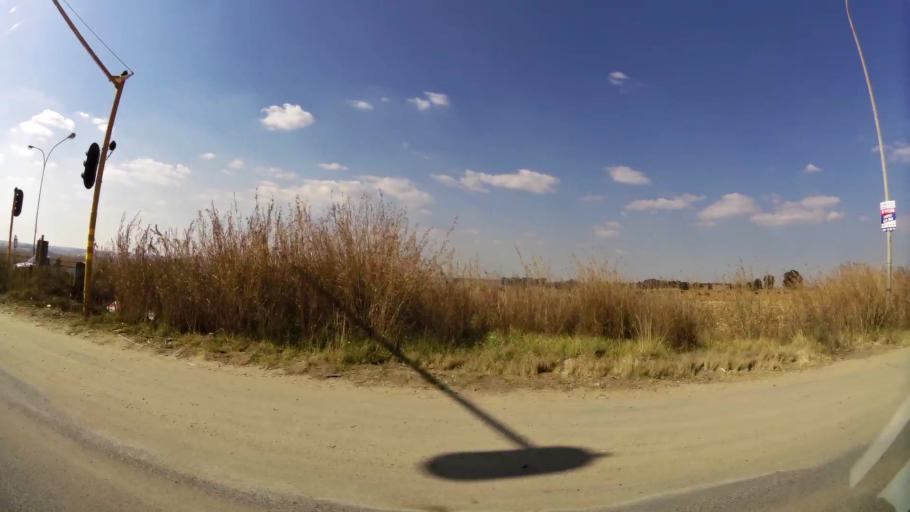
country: ZA
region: Gauteng
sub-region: Ekurhuleni Metropolitan Municipality
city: Tembisa
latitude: -26.0433
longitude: 28.2566
